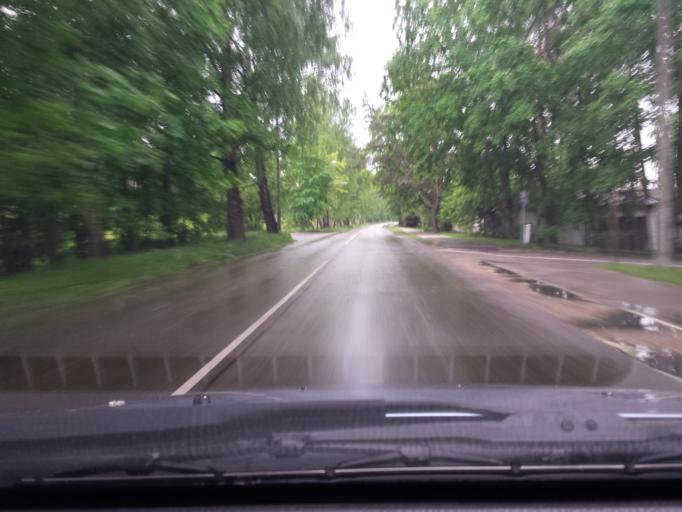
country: LV
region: Riga
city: Bolderaja
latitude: 57.0641
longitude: 24.1059
